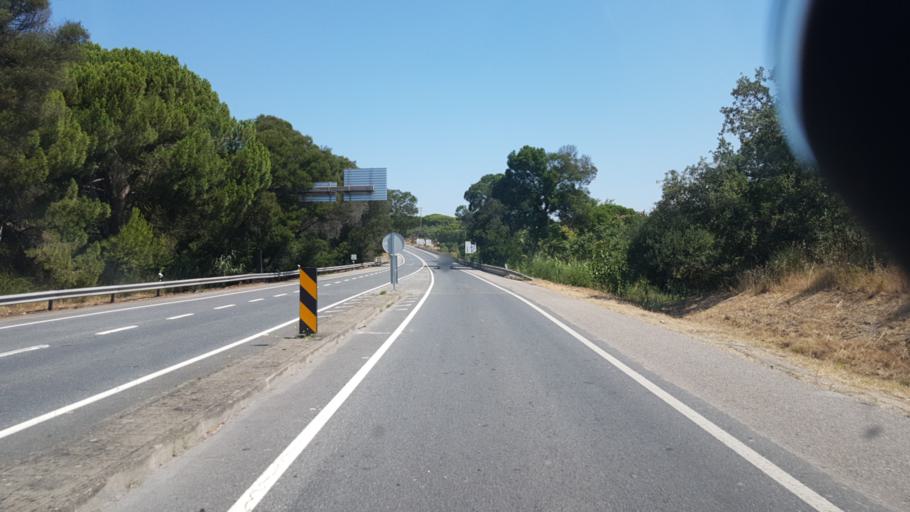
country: PT
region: Setubal
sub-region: Alcacer do Sal
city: Alcacer do Sal
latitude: 38.4048
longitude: -8.5161
